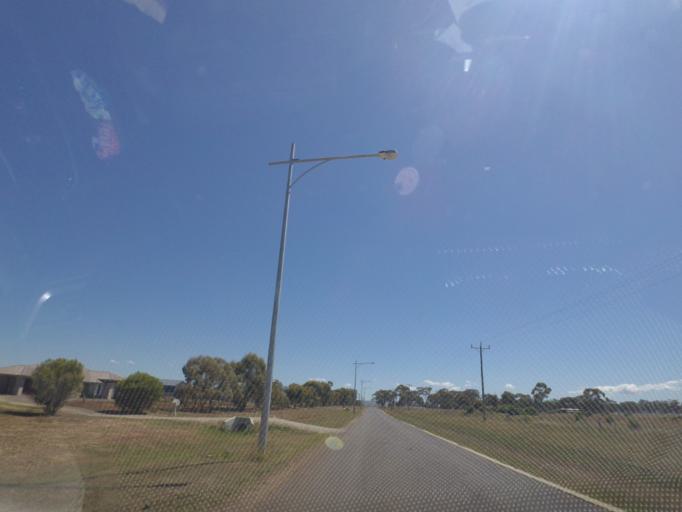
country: AU
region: Victoria
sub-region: Melton
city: Brookfield
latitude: -37.6957
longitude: 144.5060
